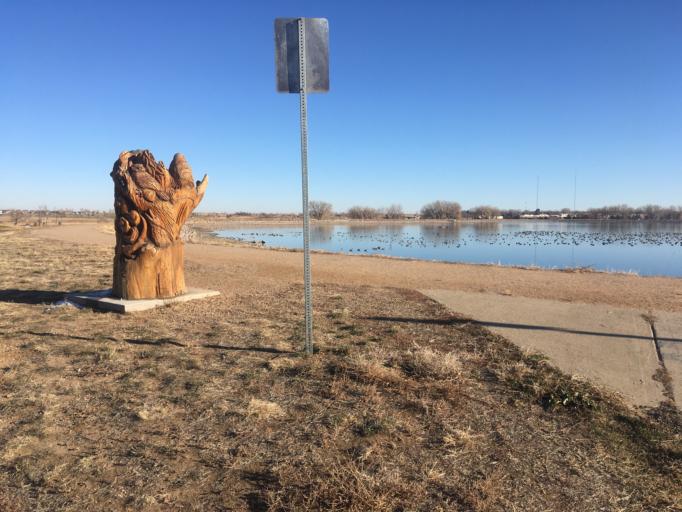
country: US
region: Colorado
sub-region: Weld County
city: Firestone
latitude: 40.1247
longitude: -104.9493
